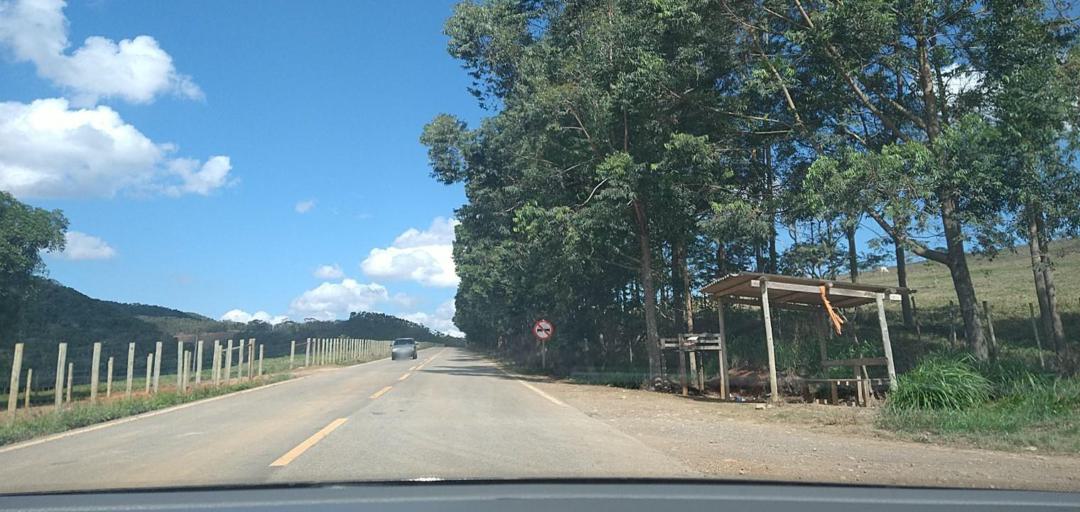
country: BR
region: Minas Gerais
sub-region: Alvinopolis
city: Alvinopolis
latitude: -20.0181
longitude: -43.0734
